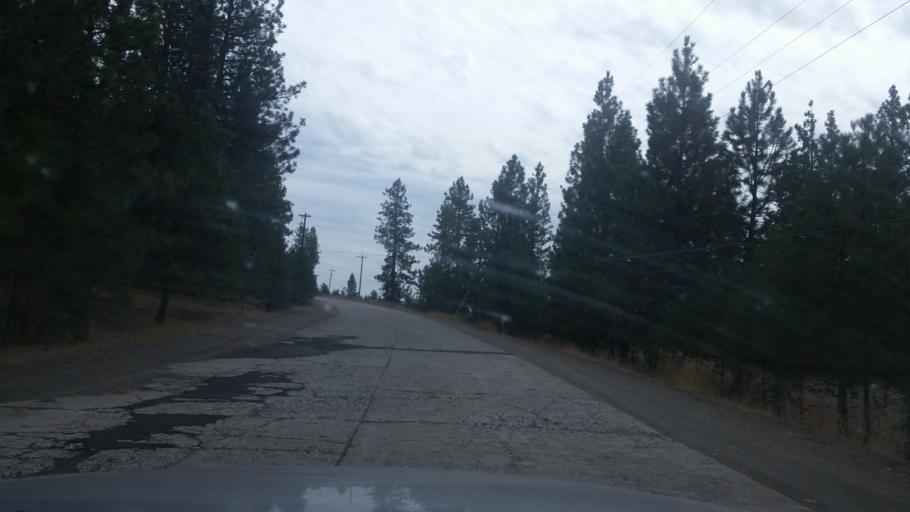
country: US
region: Washington
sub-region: Spokane County
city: Cheney
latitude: 47.5576
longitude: -117.5961
